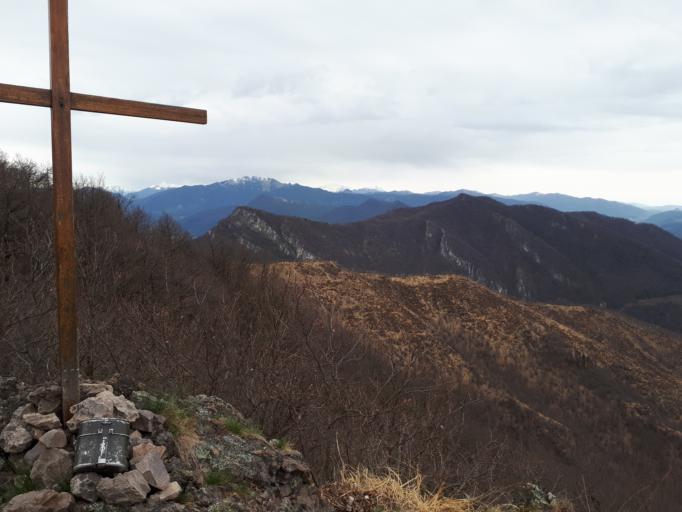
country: IT
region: Lombardy
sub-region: Provincia di Varese
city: Valganna
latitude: 45.8837
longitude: 8.8126
